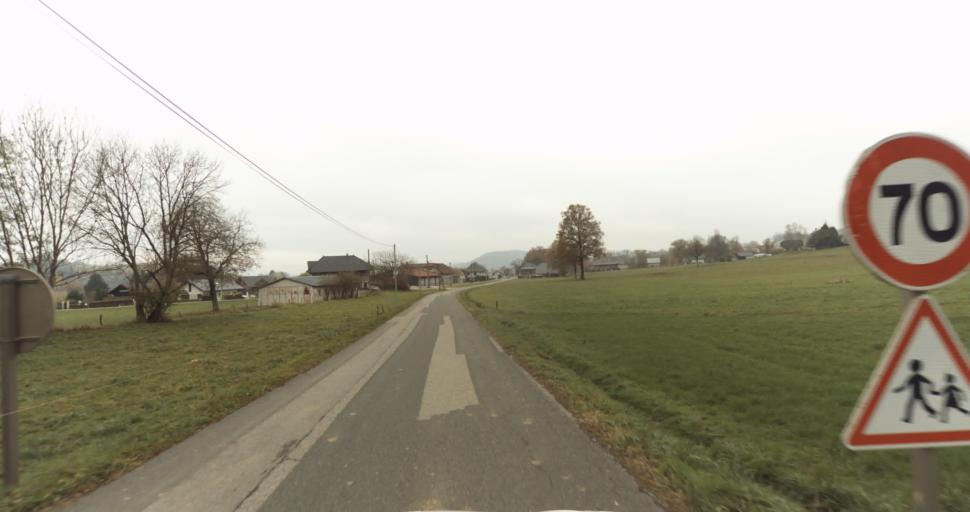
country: FR
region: Rhone-Alpes
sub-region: Departement de la Haute-Savoie
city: Alby-sur-Cheran
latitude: 45.8013
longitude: 6.0339
